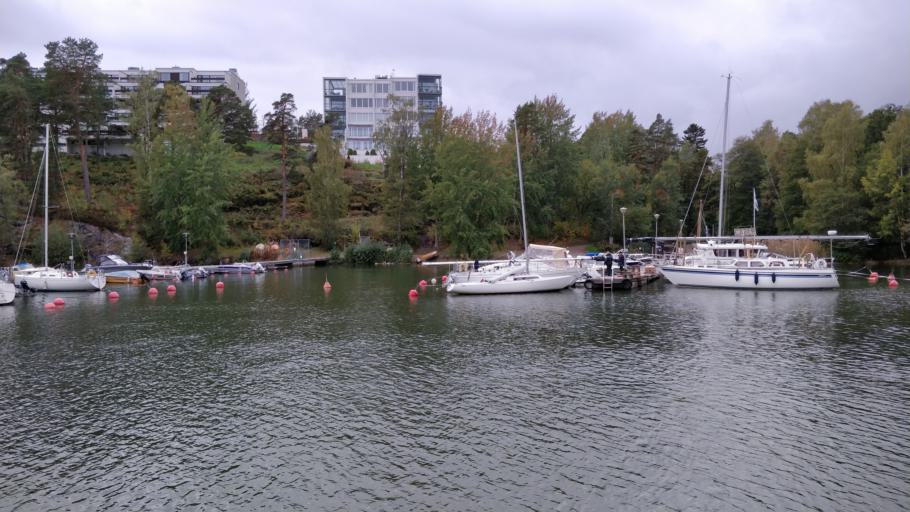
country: FI
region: Uusimaa
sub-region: Helsinki
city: Vantaa
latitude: 60.1833
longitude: 25.0649
